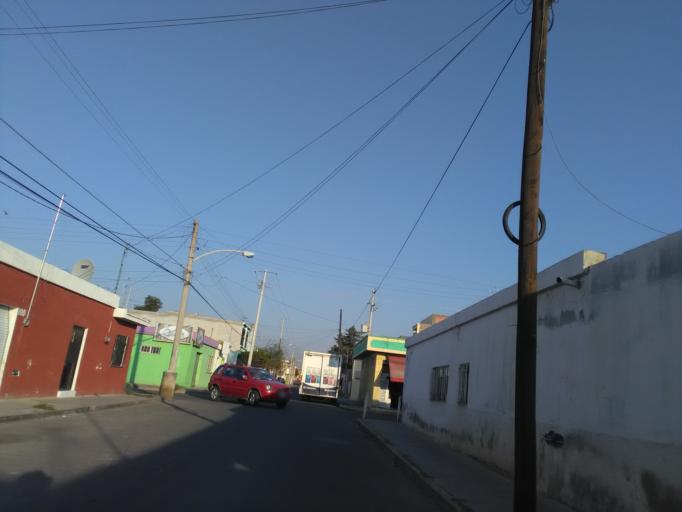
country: MX
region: Durango
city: Victoria de Durango
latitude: 24.0383
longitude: -104.6394
